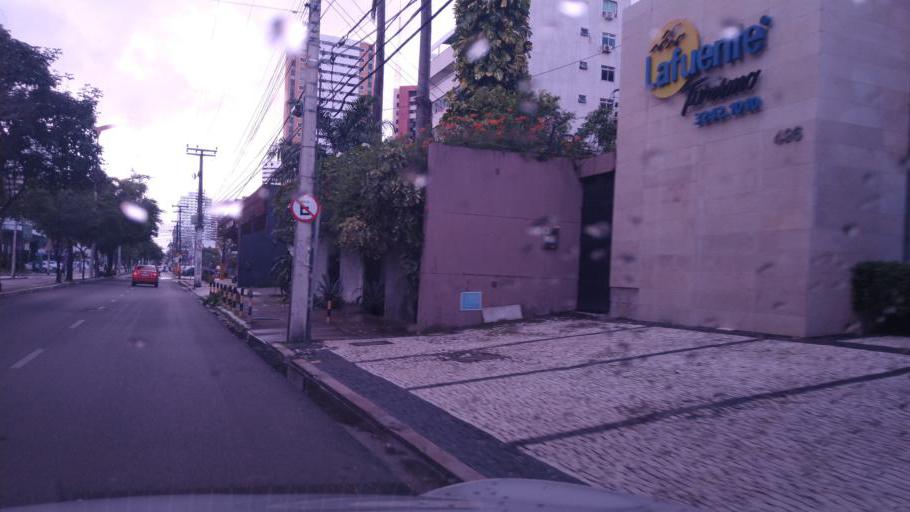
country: BR
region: Ceara
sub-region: Fortaleza
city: Fortaleza
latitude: -3.7321
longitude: -38.4917
